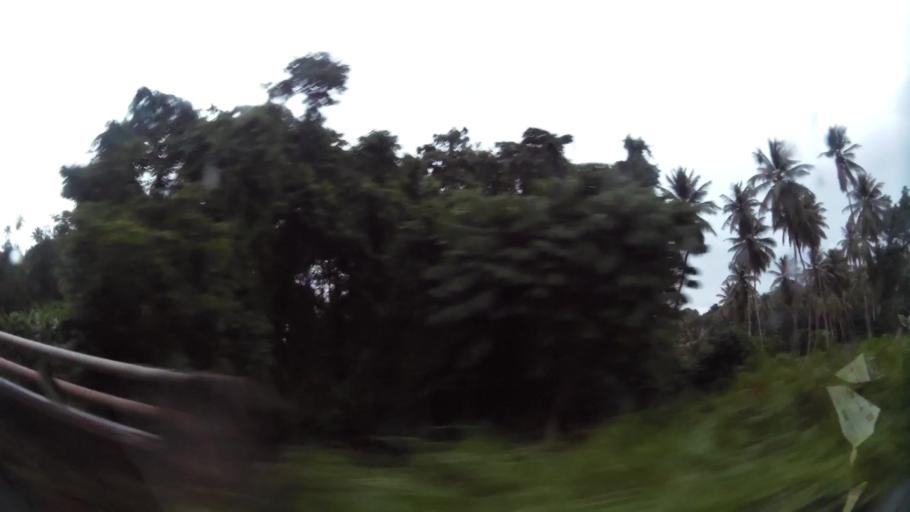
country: DM
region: Saint Andrew
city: Wesley
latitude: 15.5538
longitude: -61.3074
